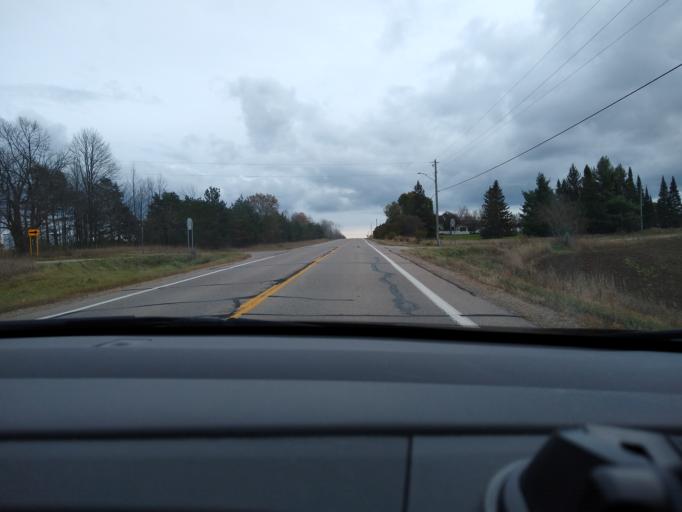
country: US
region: Michigan
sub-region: Delta County
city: Escanaba
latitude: 45.7449
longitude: -87.2749
